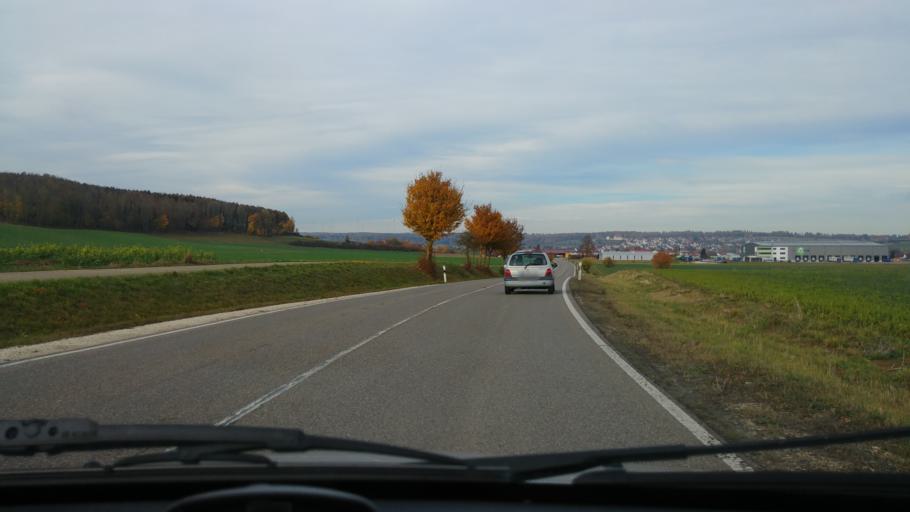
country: DE
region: Bavaria
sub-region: Swabia
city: Bachhagel
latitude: 48.6313
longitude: 10.2945
